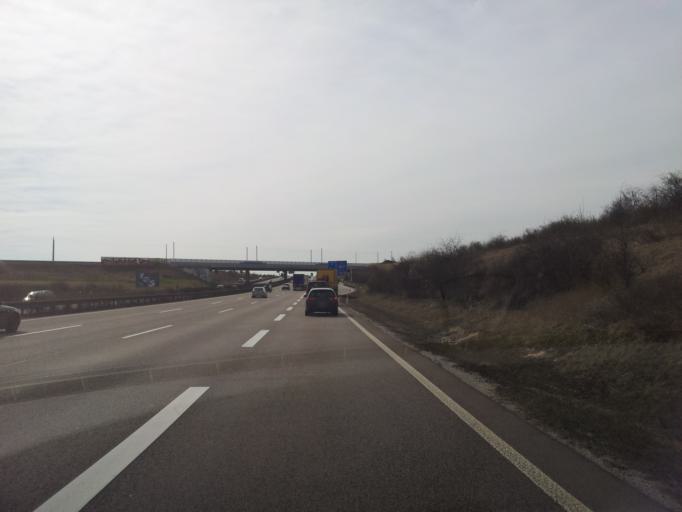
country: DE
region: Thuringia
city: Ichtershausen
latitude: 50.8963
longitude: 10.9627
